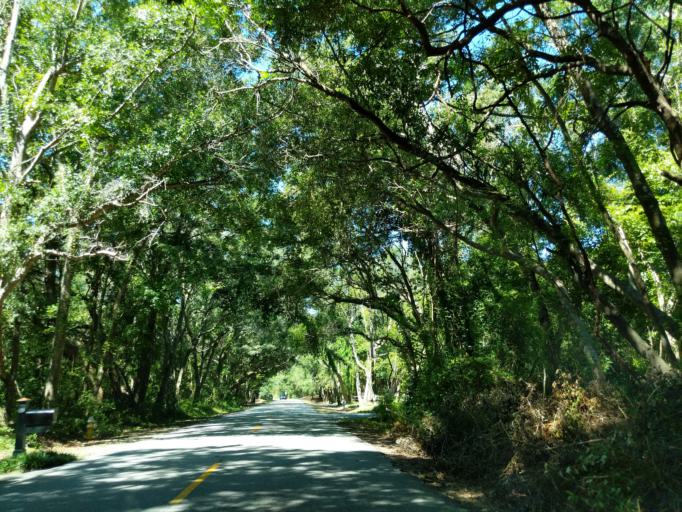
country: US
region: South Carolina
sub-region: Charleston County
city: Folly Beach
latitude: 32.7048
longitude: -79.9453
